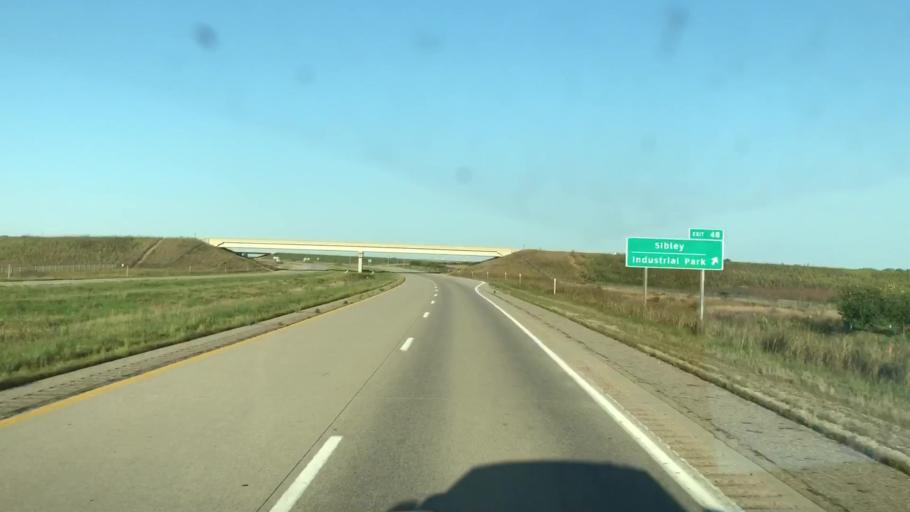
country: US
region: Iowa
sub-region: Osceola County
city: Sibley
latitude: 43.3845
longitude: -95.7388
